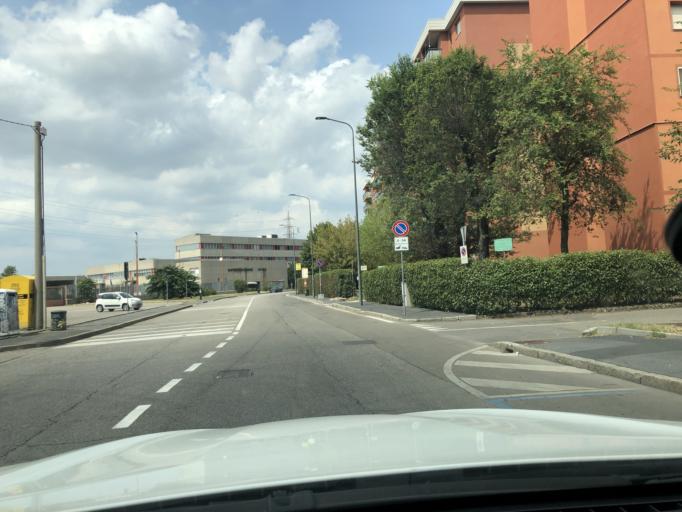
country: IT
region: Lombardy
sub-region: Citta metropolitana di Milano
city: Pero
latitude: 45.5014
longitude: 9.0951
